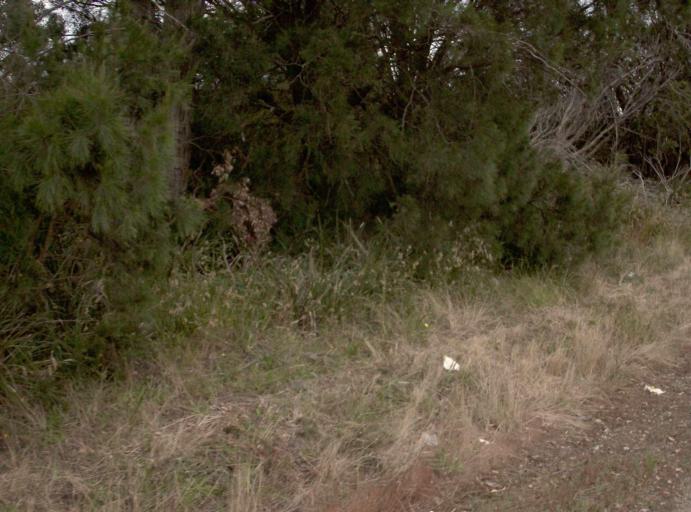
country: AU
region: Victoria
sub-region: East Gippsland
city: Bairnsdale
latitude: -37.9365
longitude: 147.5298
